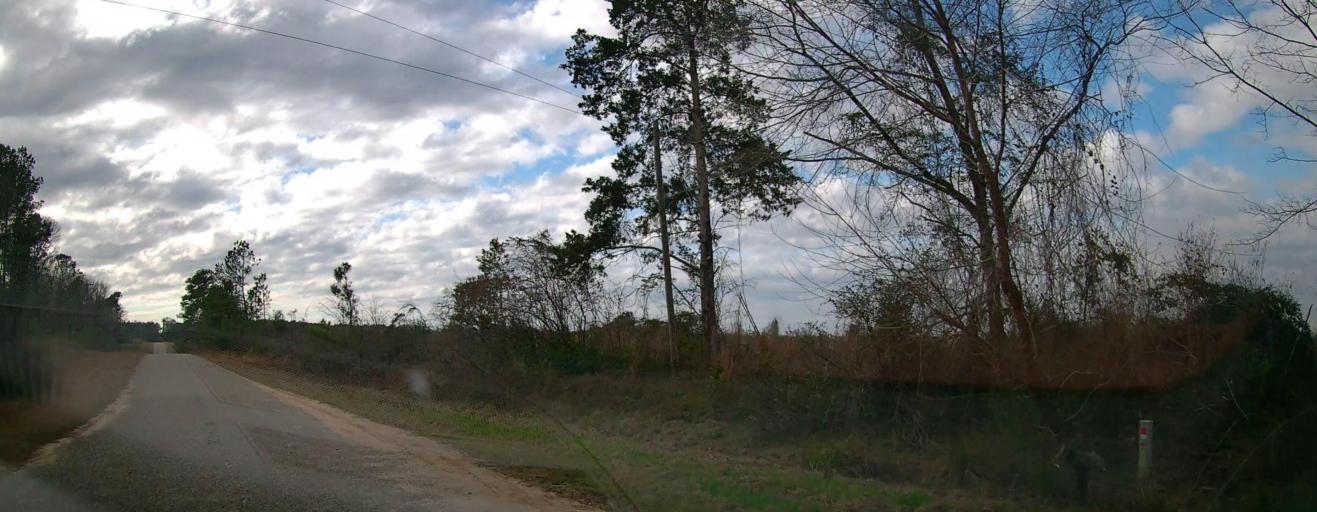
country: US
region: Georgia
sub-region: Marion County
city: Buena Vista
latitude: 32.4356
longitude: -84.4207
